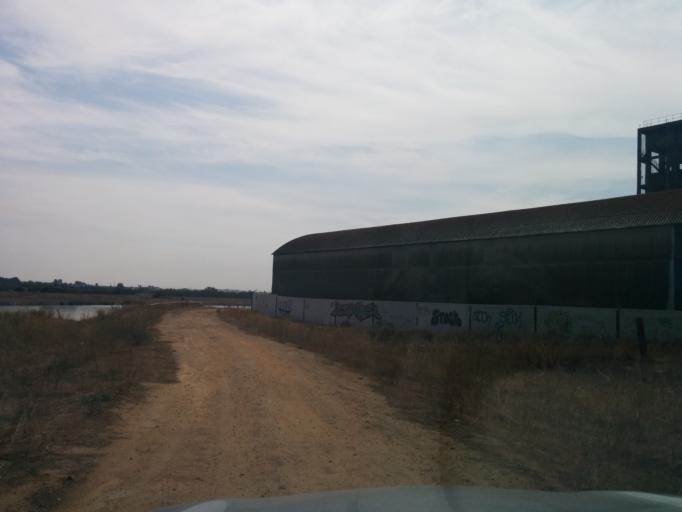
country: ES
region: Andalusia
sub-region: Provincia de Sevilla
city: Gelves
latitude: 37.3263
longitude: -5.9932
